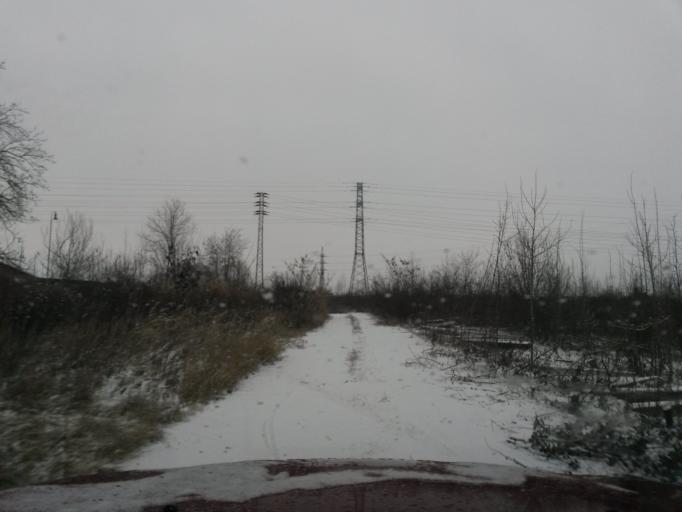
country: SK
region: Kosicky
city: Moldava nad Bodvou
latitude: 48.5980
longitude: 21.0046
